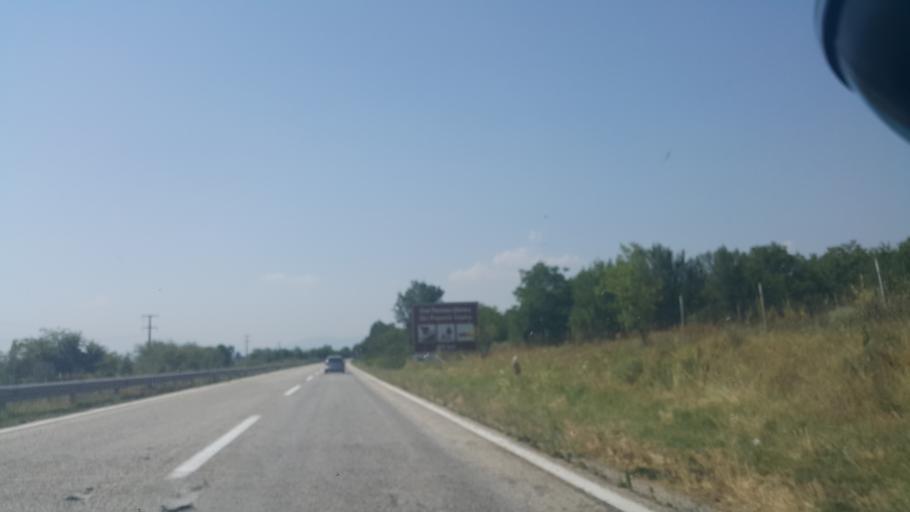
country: MK
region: Petrovec
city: Petrovec
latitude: 41.9112
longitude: 21.6465
